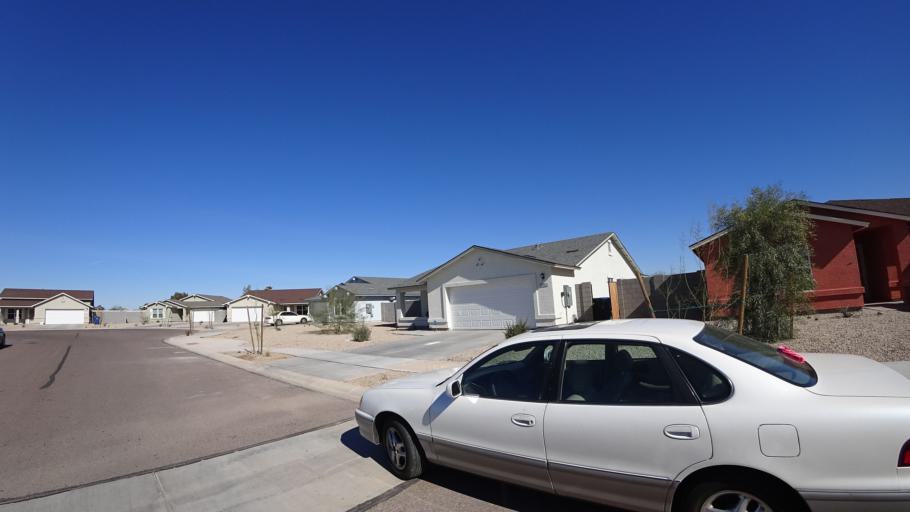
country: US
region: Arizona
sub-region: Maricopa County
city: Avondale
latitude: 33.4153
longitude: -112.3304
